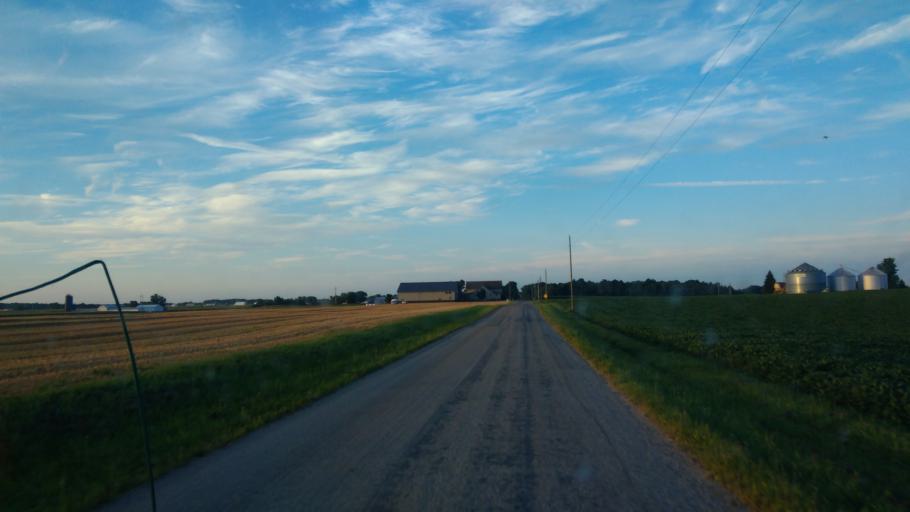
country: US
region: Indiana
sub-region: Adams County
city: Berne
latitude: 40.6673
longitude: -85.0229
